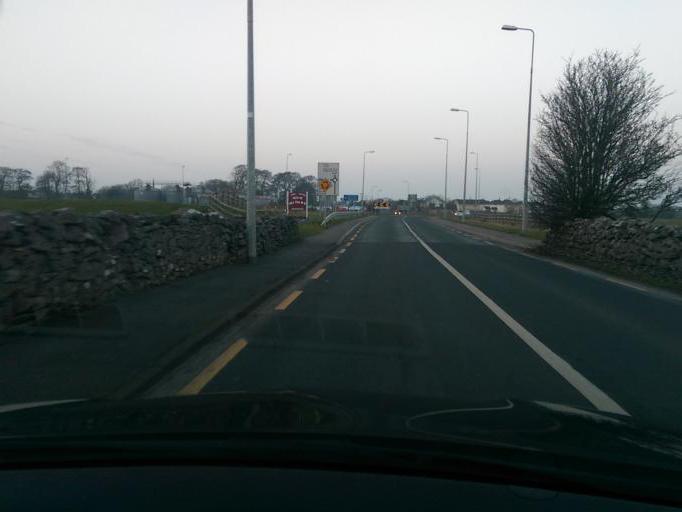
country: IE
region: Connaught
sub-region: County Galway
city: Athenry
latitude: 53.2925
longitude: -8.7436
